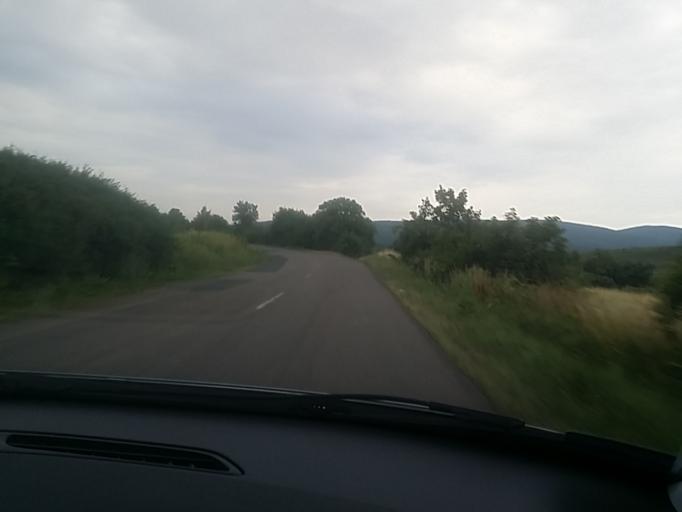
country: HU
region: Nograd
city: Paszto
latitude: 47.9072
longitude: 19.6650
